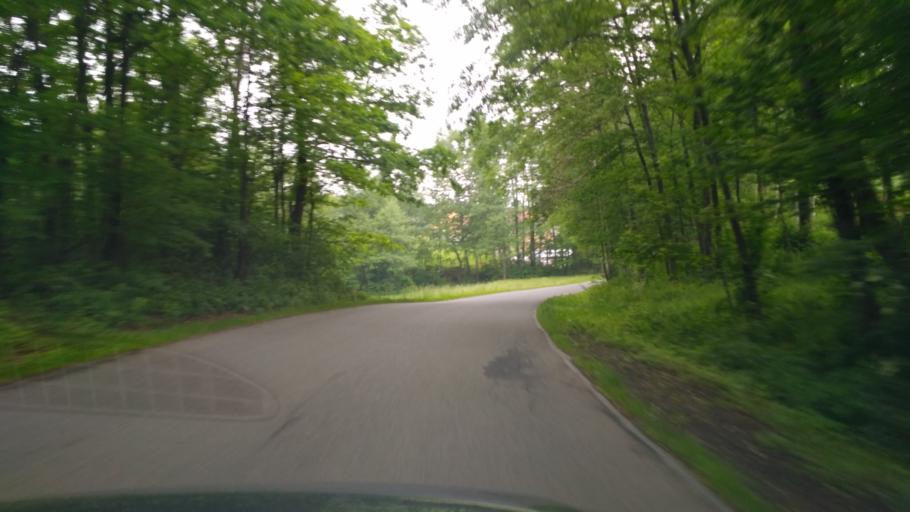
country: PL
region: Subcarpathian Voivodeship
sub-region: Powiat ropczycko-sedziszowski
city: Zagorzyce
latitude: 50.0115
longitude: 21.6766
